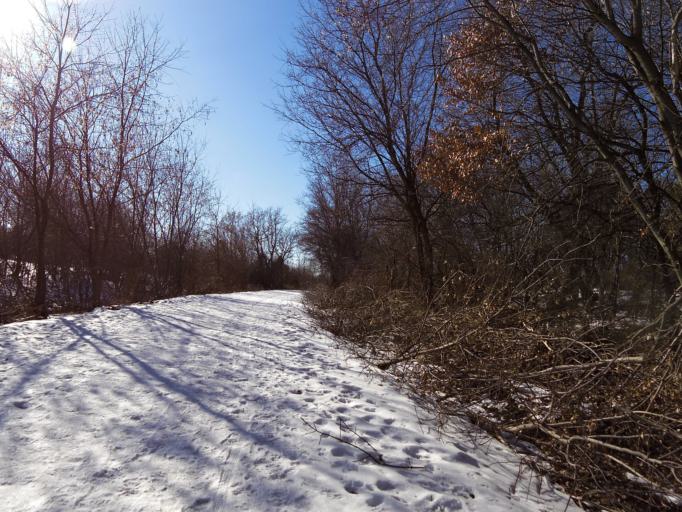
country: US
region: Minnesota
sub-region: Washington County
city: Stillwater
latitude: 45.0710
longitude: -92.8371
